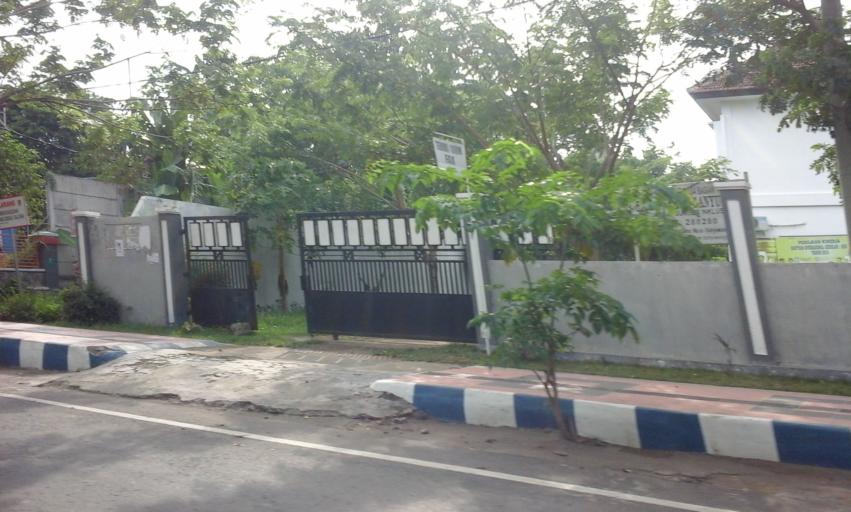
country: ID
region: East Java
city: Cungking
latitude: -8.2115
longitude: 114.3506
